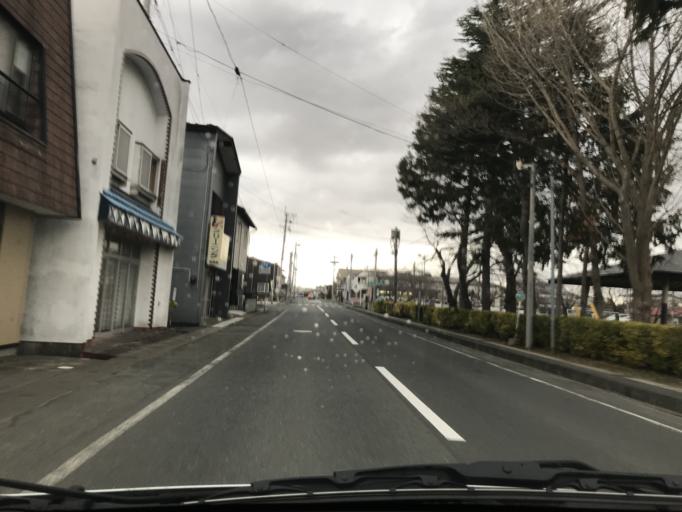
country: JP
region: Iwate
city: Mizusawa
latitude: 39.1384
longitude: 141.1573
